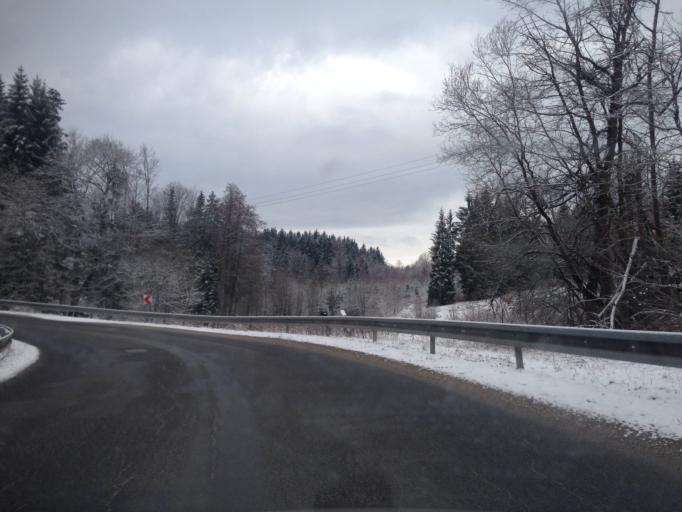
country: CZ
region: Liberecky
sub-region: Okres Semily
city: Ponikla
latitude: 50.6463
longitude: 15.4355
